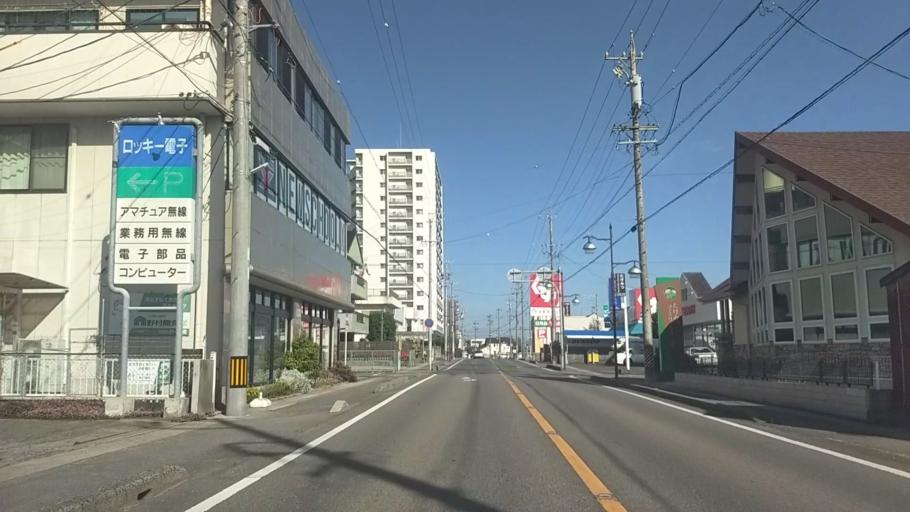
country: JP
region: Aichi
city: Anjo
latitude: 34.9539
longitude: 137.0858
